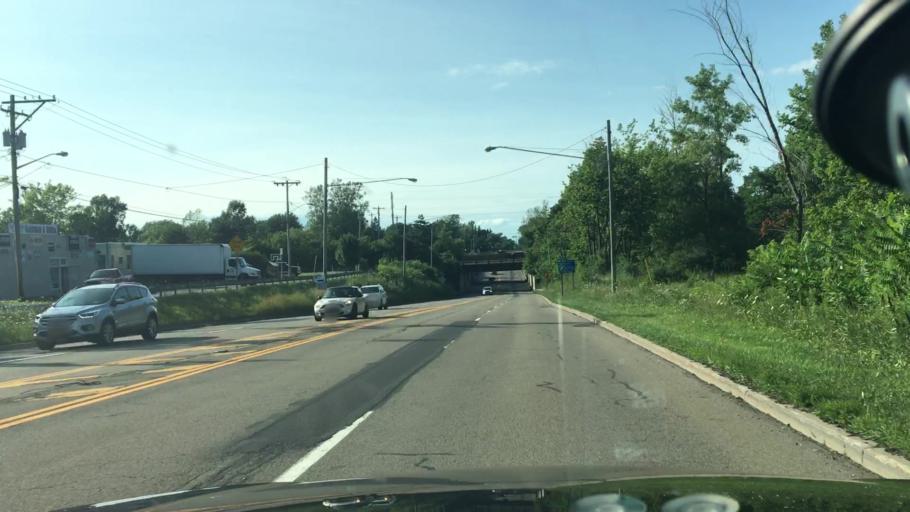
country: US
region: New York
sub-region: Erie County
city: Wanakah
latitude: 42.7630
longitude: -78.8632
